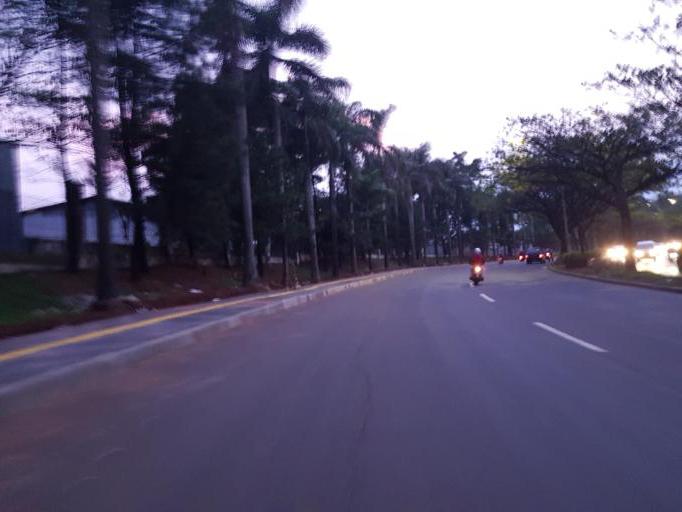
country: ID
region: West Java
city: Serpong
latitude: -6.3306
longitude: 106.6805
